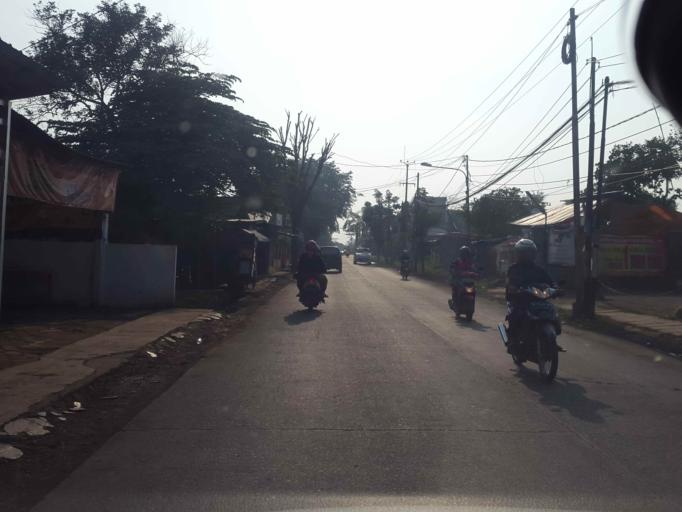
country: ID
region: West Java
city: Bekasi
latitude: -6.3149
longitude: 106.9981
